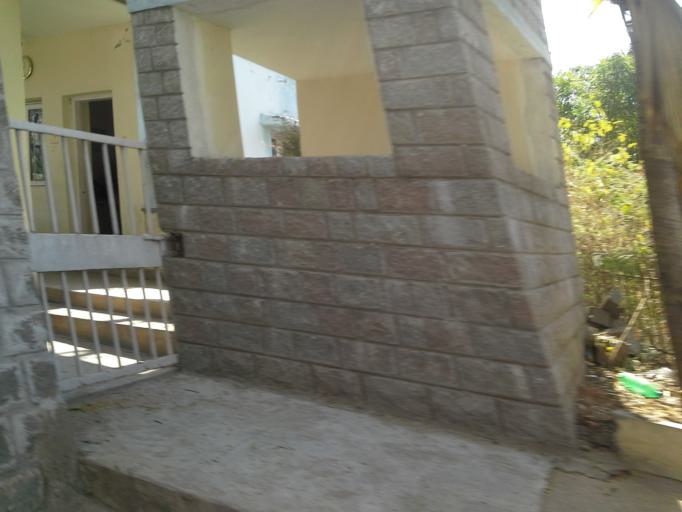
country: IN
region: Telangana
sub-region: Hyderabad
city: Hyderabad
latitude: 17.3111
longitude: 78.4091
